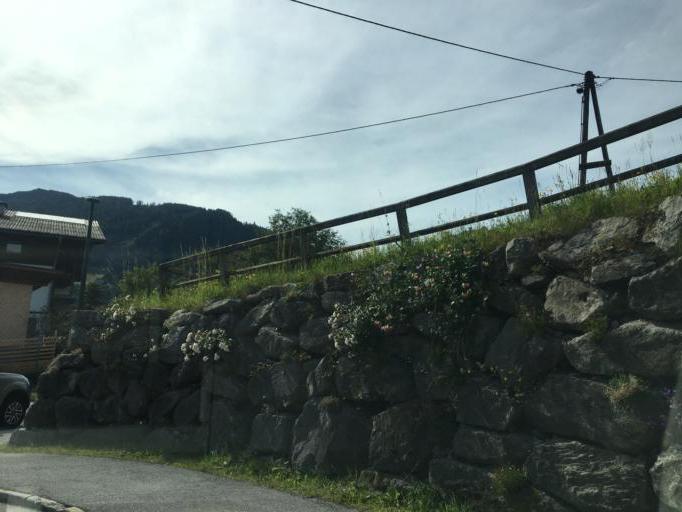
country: AT
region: Styria
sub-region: Politischer Bezirk Liezen
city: Schladming
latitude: 47.3830
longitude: 13.6727
